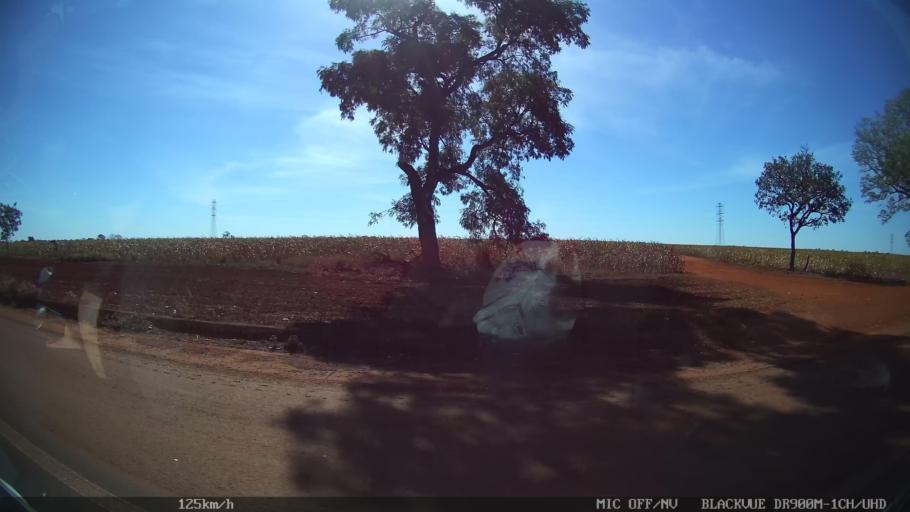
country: BR
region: Sao Paulo
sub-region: Guaira
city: Guaira
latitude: -20.4445
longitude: -48.3699
